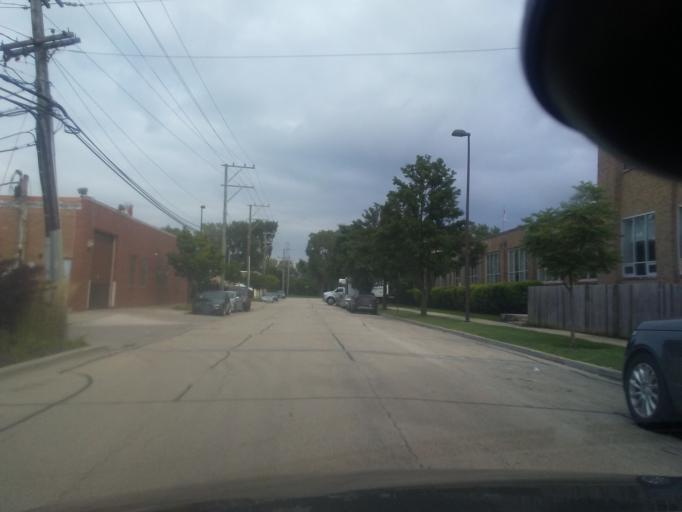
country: US
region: Illinois
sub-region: Cook County
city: Skokie
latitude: 42.0300
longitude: -87.7132
